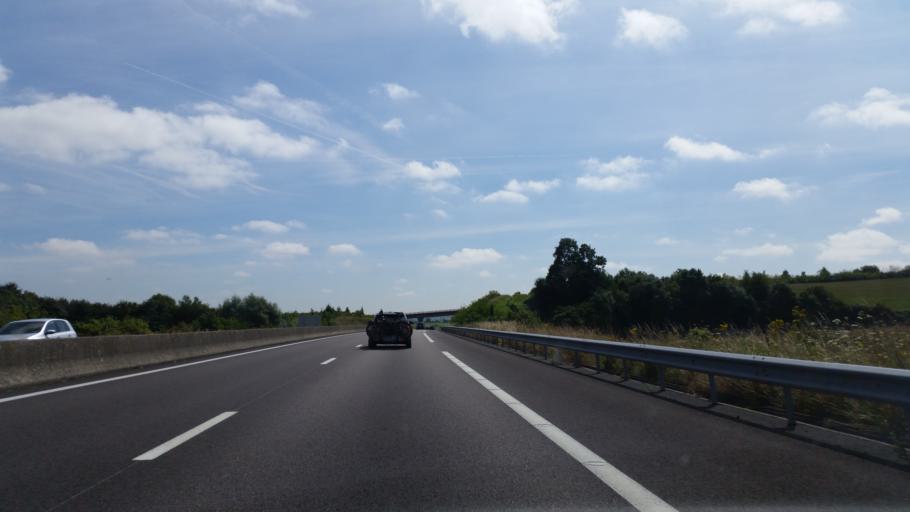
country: FR
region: Haute-Normandie
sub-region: Departement de la Seine-Maritime
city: Neufchatel-en-Bray
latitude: 49.7460
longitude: 1.5248
